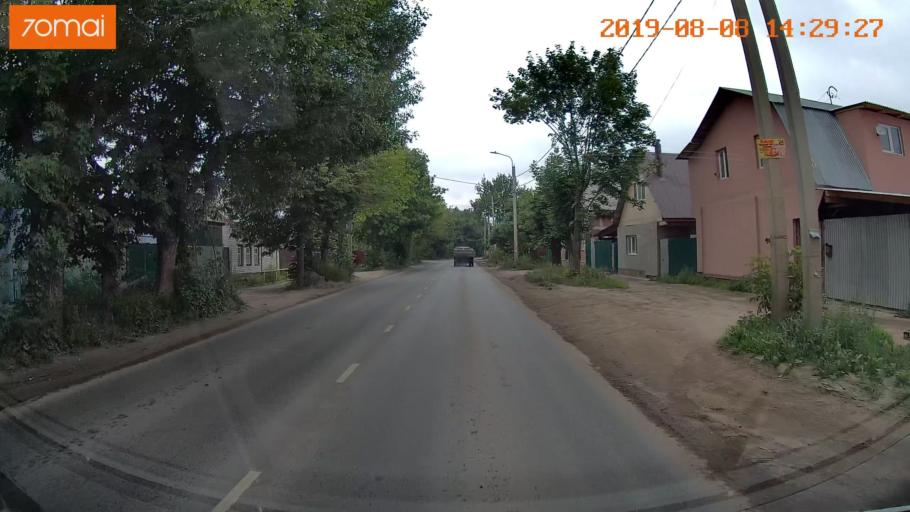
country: RU
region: Ivanovo
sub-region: Gorod Ivanovo
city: Ivanovo
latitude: 56.9939
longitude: 40.9523
